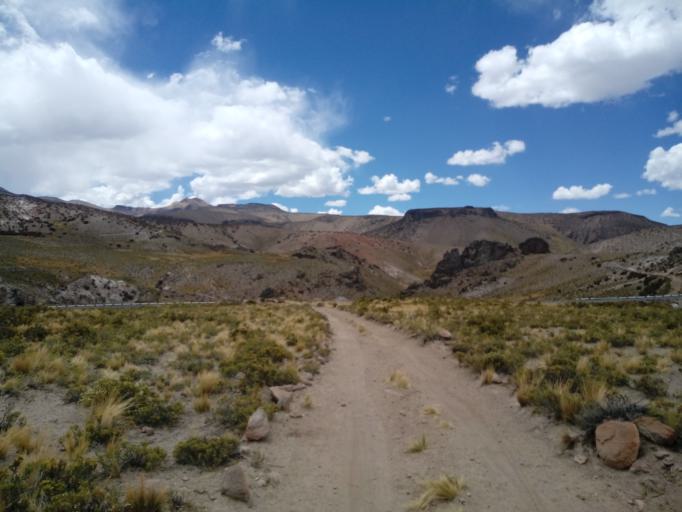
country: PE
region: Puno
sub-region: El Collao
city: Mazo Cruz
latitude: -16.7644
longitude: -69.8904
